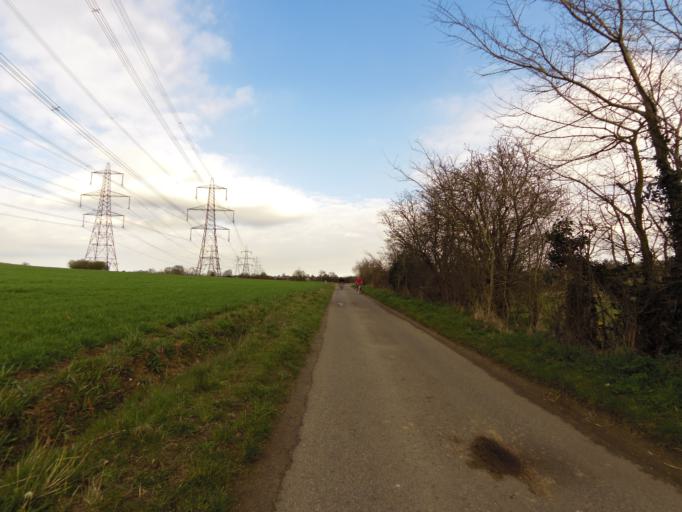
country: GB
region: England
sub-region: Suffolk
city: Ipswich
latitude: 52.0920
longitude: 1.1382
